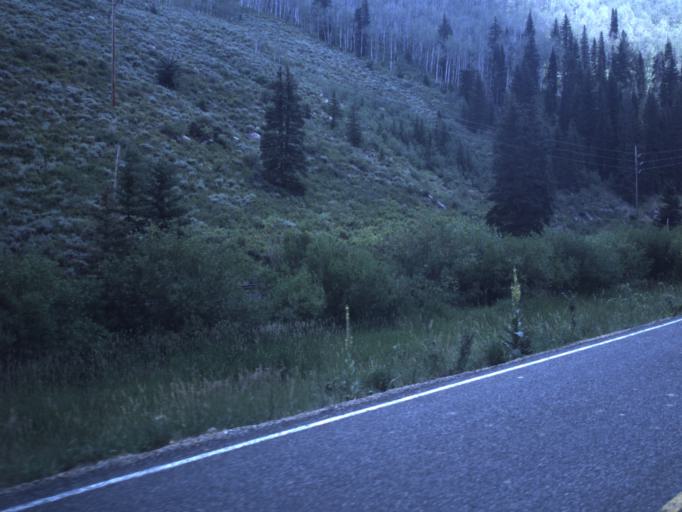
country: US
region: Utah
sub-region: Sanpete County
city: Fairview
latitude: 39.6748
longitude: -111.1559
